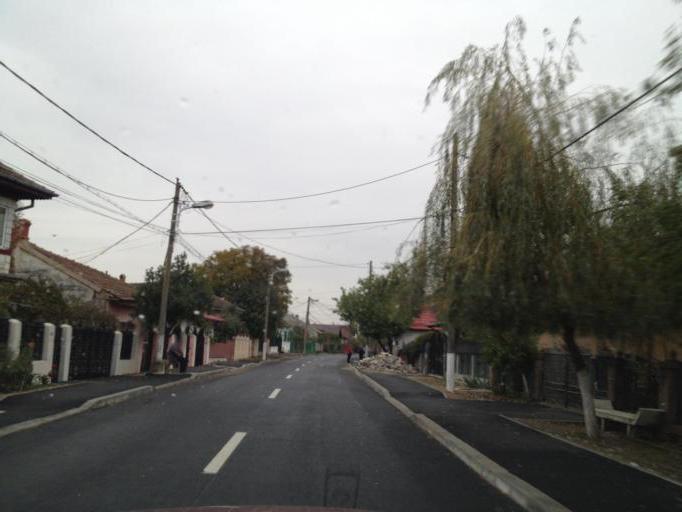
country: RO
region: Dolj
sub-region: Comuna Bucovat
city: Bucovat
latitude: 44.3028
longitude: 23.7529
